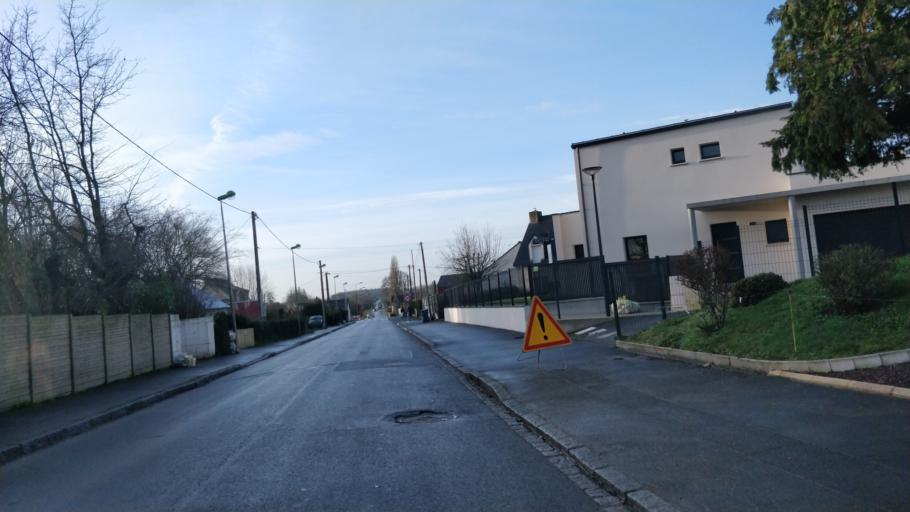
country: FR
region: Brittany
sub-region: Departement d'Ille-et-Vilaine
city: Liffre
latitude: 48.2094
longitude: -1.5092
